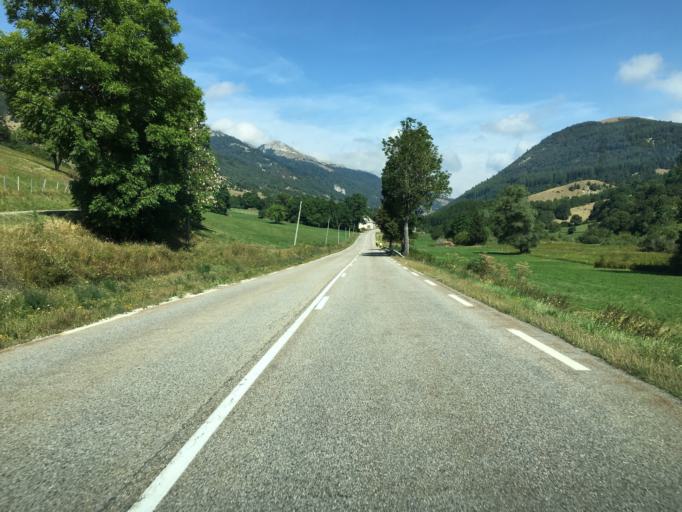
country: FR
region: Rhone-Alpes
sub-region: Departement de l'Isere
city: Mens
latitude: 44.6880
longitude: 5.6883
